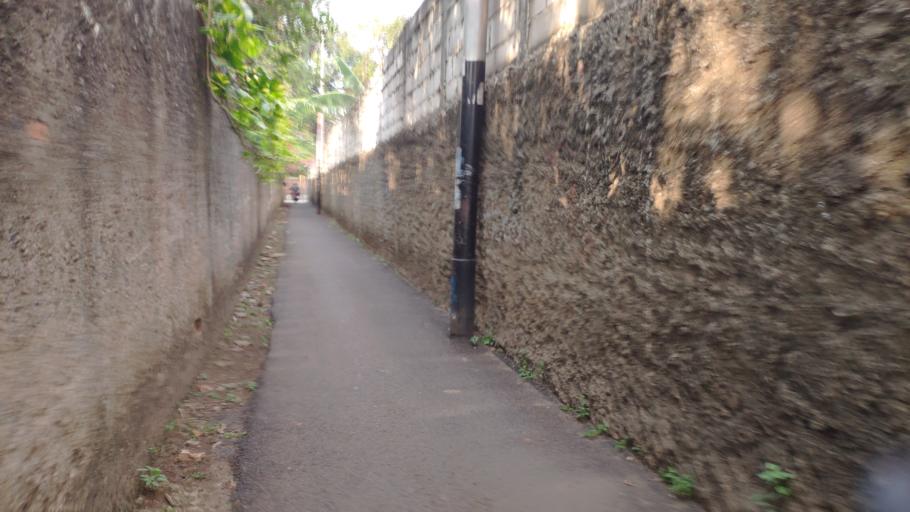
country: ID
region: West Java
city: Pamulang
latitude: -6.3109
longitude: 106.7974
